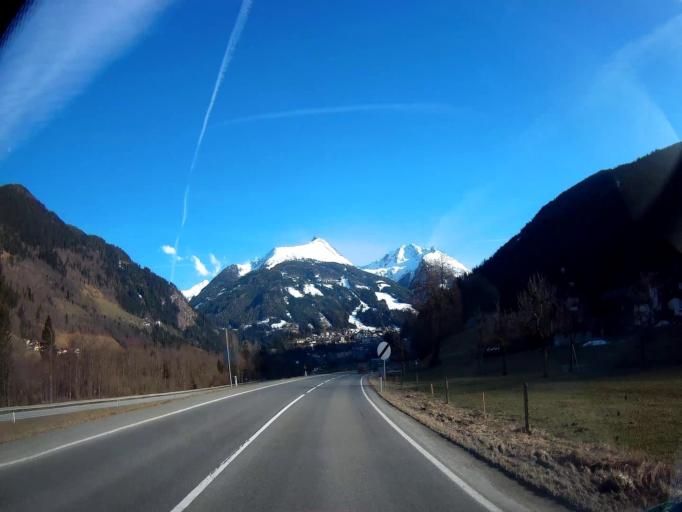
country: AT
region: Salzburg
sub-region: Politischer Bezirk Sankt Johann im Pongau
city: Bad Gastein
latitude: 47.1427
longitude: 13.1221
